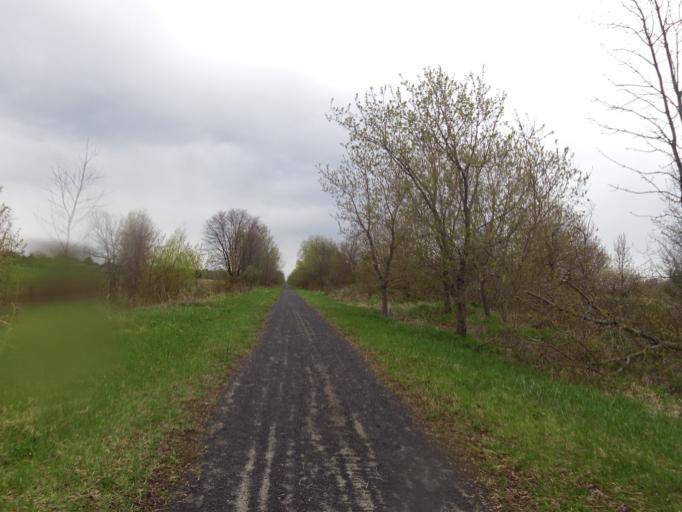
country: CA
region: Ontario
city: Bourget
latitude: 45.4393
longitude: -75.1863
